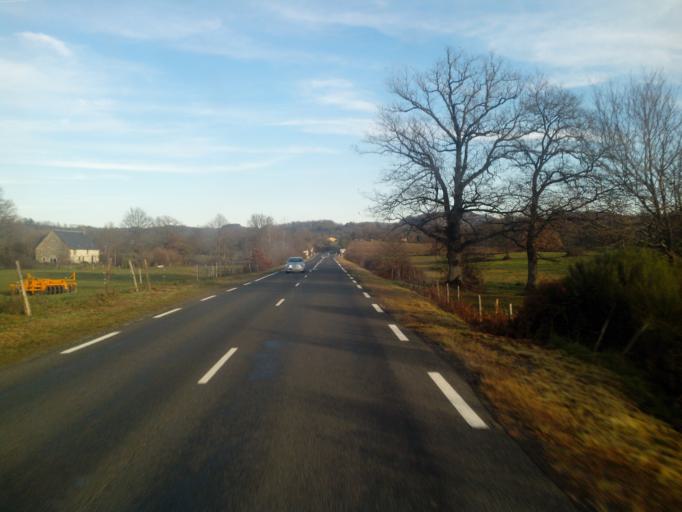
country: FR
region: Limousin
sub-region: Departement de la Correze
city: Bort-les-Orgues
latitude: 45.3569
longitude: 2.5031
